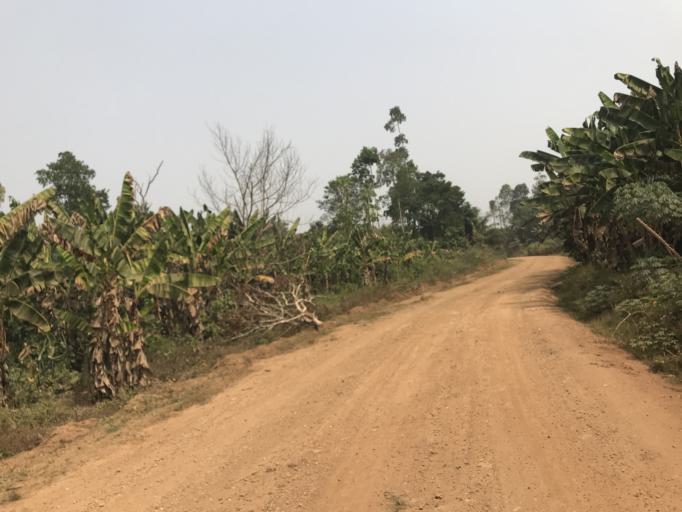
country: NG
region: Osun
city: Ifetedo
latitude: 7.0285
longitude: 4.4482
